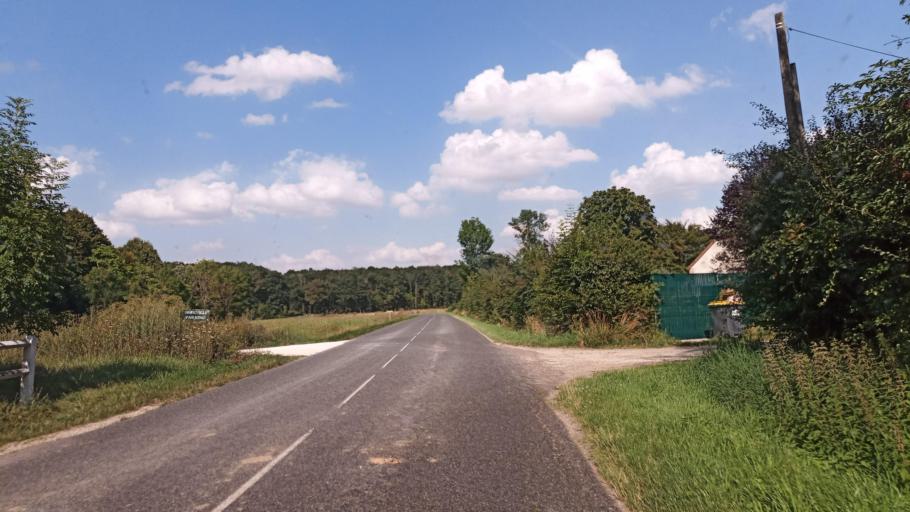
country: FR
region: Bourgogne
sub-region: Departement de l'Yonne
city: Saint-Valerien
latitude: 48.1562
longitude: 3.0957
